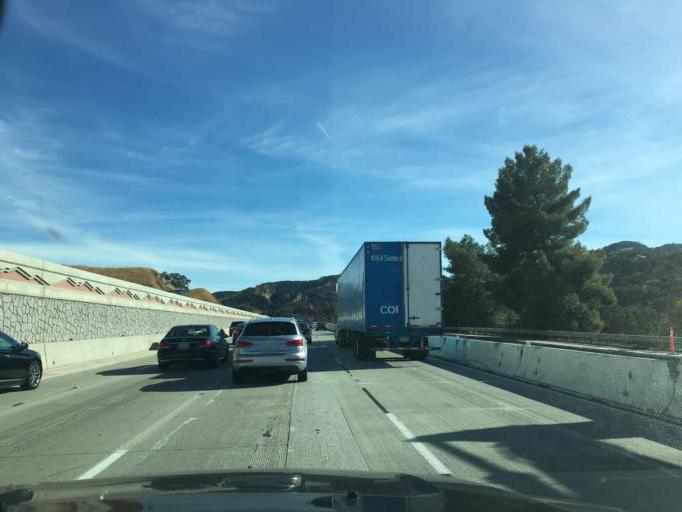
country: US
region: California
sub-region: Los Angeles County
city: Santa Clarita
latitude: 34.3556
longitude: -118.5511
